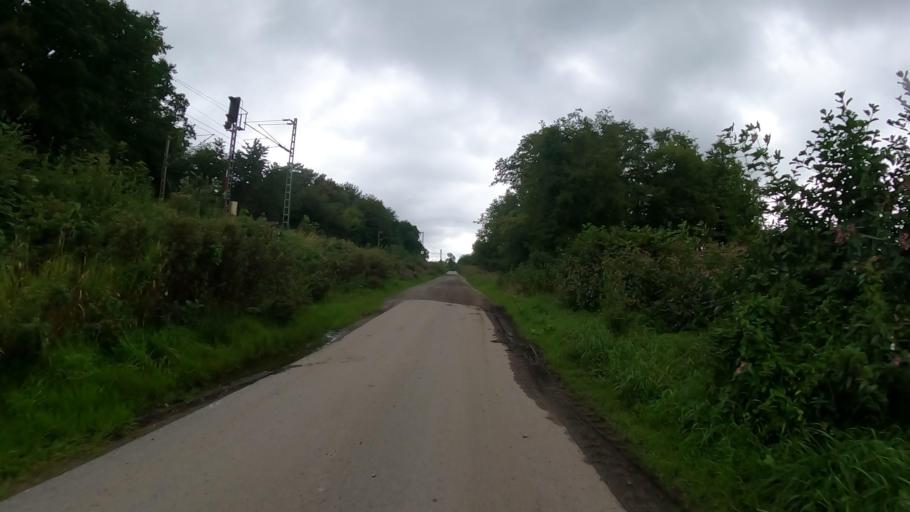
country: DE
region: Lower Saxony
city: Agathenburg
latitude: 53.5601
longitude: 9.5398
